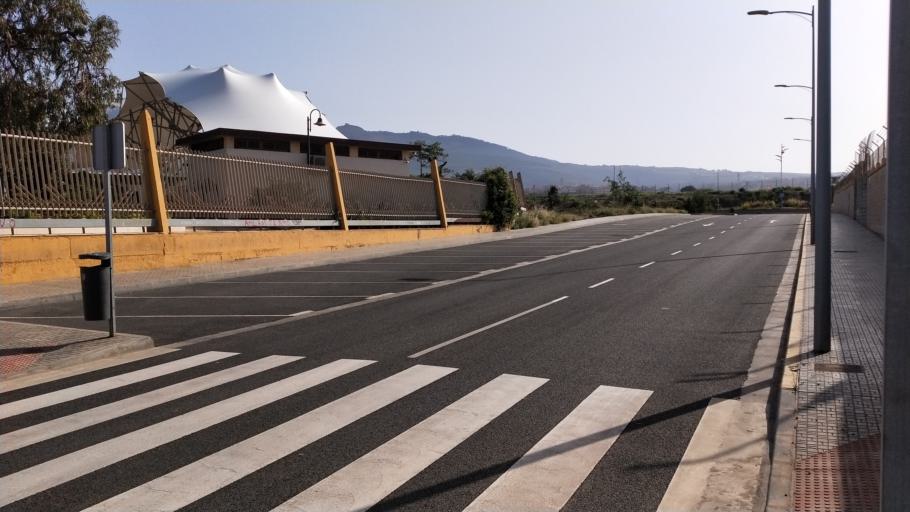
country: ES
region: Melilla
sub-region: Melilla
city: Melilla
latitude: 35.2774
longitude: -2.9507
